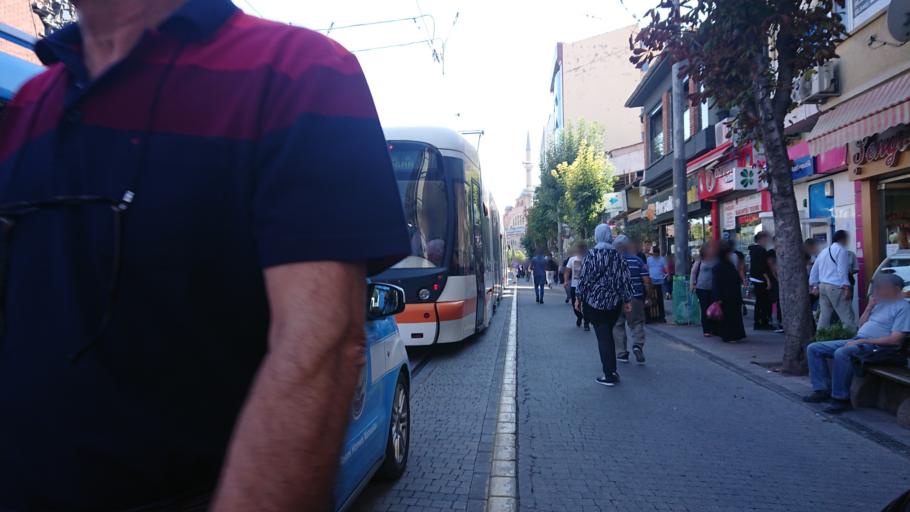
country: TR
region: Eskisehir
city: Eskisehir
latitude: 39.7732
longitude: 30.5174
